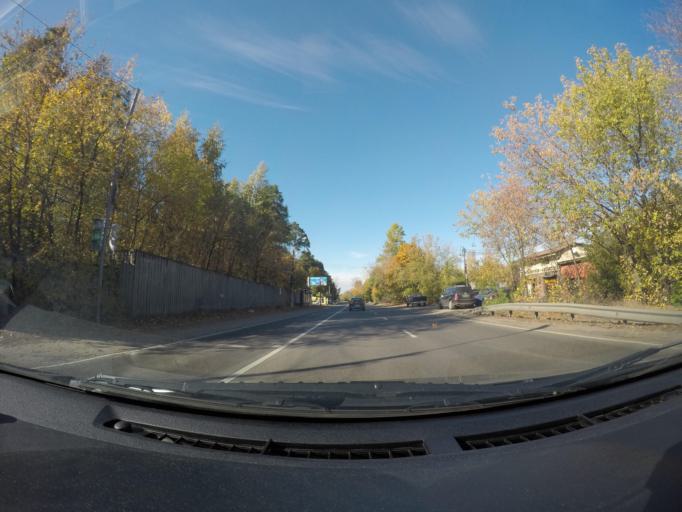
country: RU
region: Moskovskaya
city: Udel'naya
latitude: 55.6272
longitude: 38.0006
